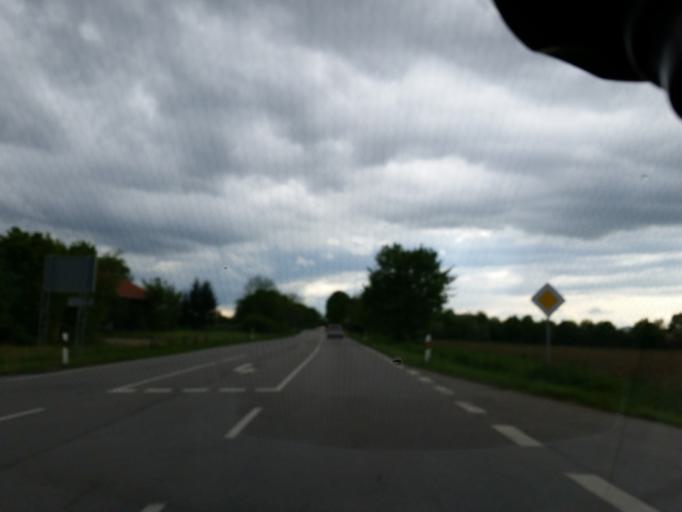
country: DE
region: Bavaria
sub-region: Upper Bavaria
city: Landsberied
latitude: 48.1692
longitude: 11.1644
